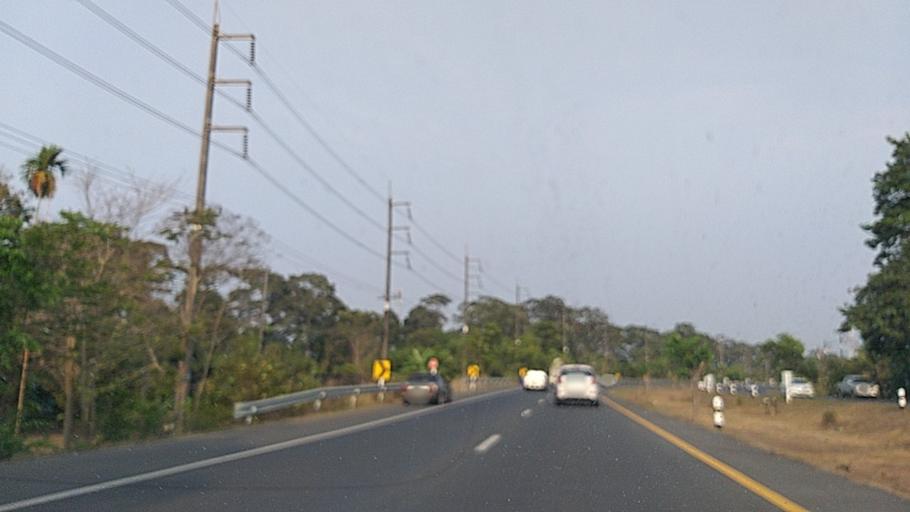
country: TH
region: Chanthaburi
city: Khlung
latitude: 12.4572
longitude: 102.2669
